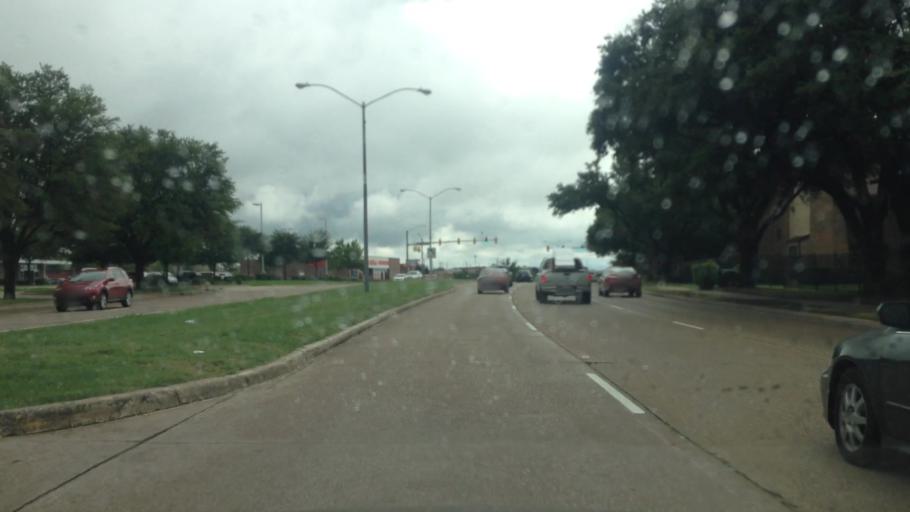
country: US
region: Texas
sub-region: Tarrant County
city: Edgecliff Village
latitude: 32.6682
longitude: -97.4002
